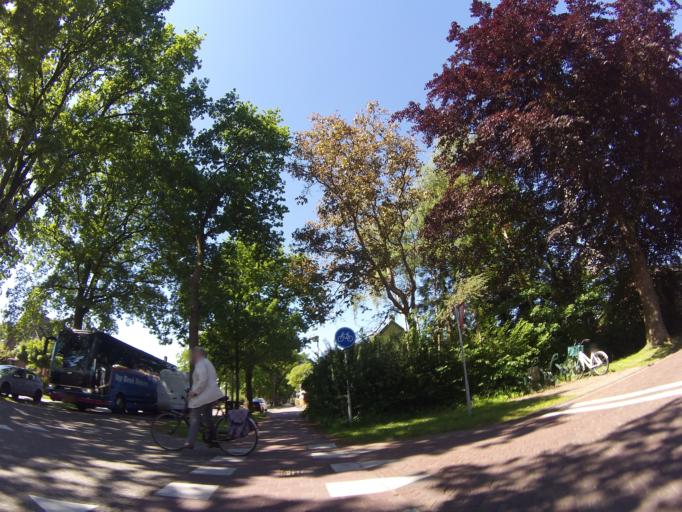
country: NL
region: Drenthe
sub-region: Gemeente Coevorden
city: Sleen
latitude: 52.7900
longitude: 6.7206
